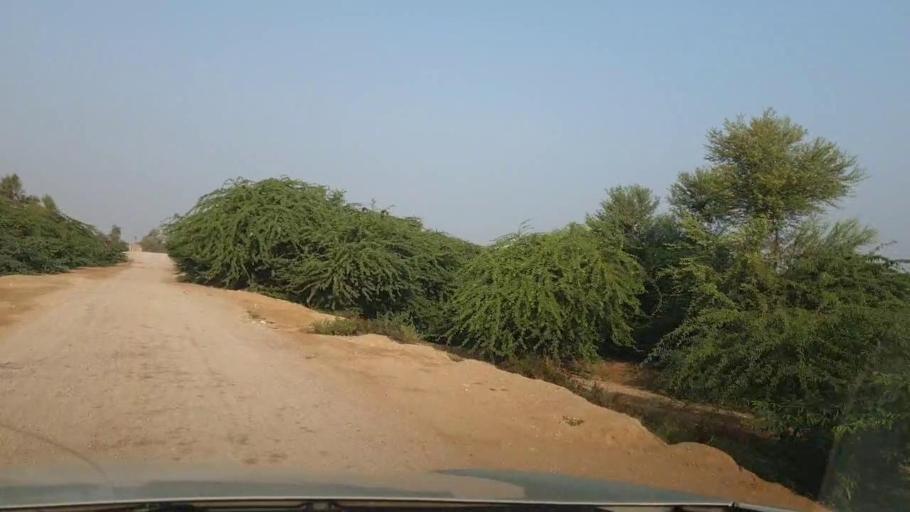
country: PK
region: Sindh
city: Sehwan
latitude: 26.3369
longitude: 67.7287
